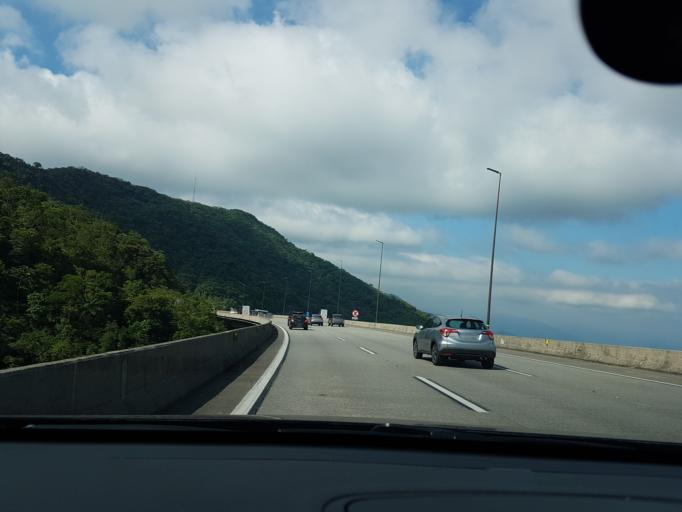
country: BR
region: Sao Paulo
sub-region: Cubatao
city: Cubatao
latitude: -23.9234
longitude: -46.5329
